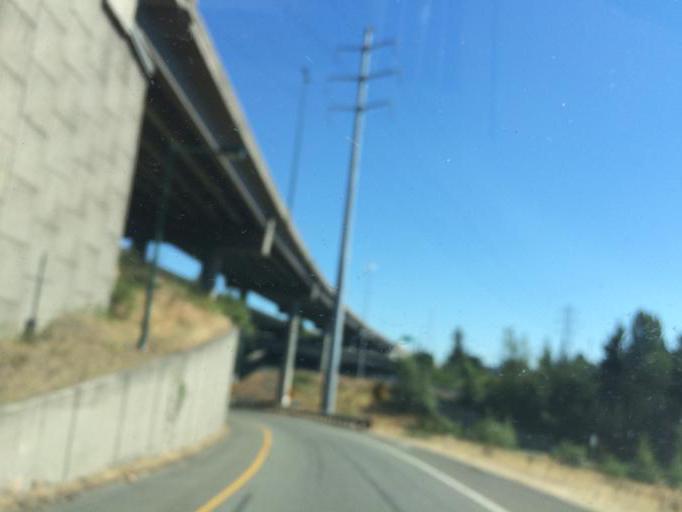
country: US
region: Washington
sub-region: King County
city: Newport
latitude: 47.5818
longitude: -122.1758
